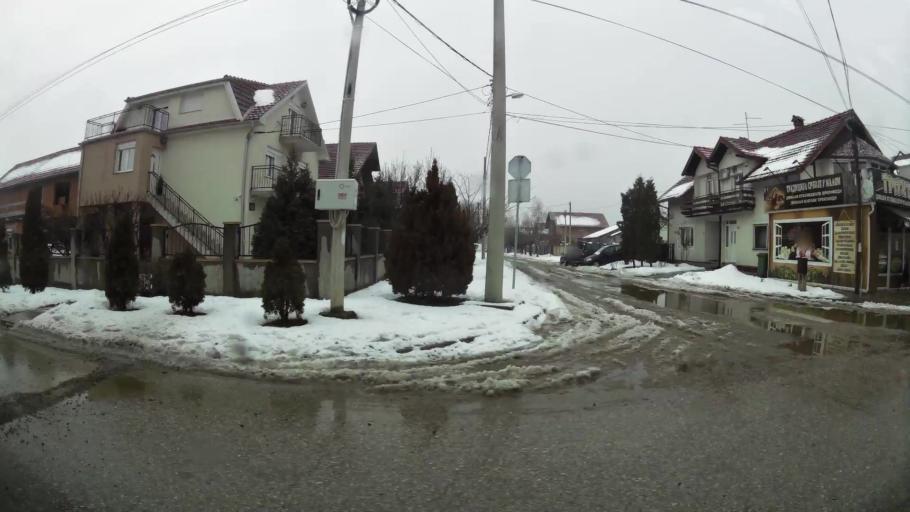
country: RS
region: Central Serbia
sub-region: Belgrade
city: Zemun
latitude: 44.8506
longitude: 20.3513
